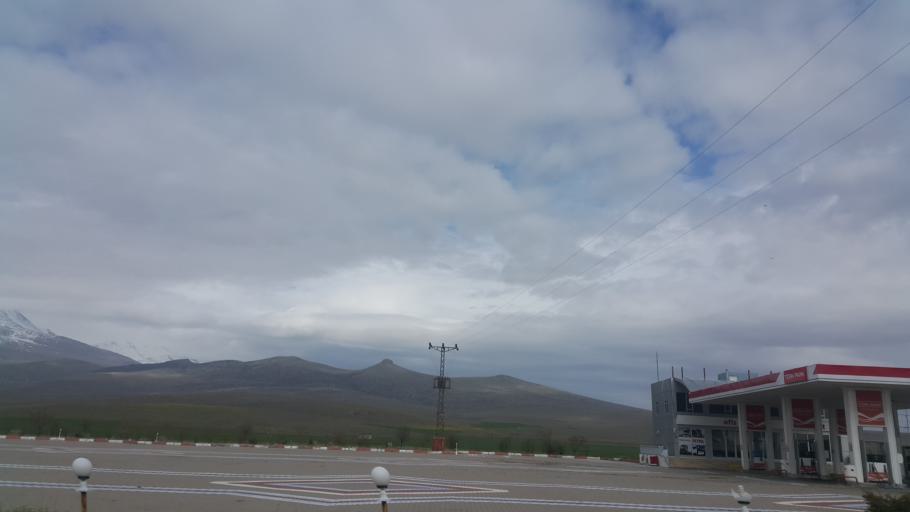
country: TR
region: Aksaray
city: Taspinar
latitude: 38.0585
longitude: 34.0322
